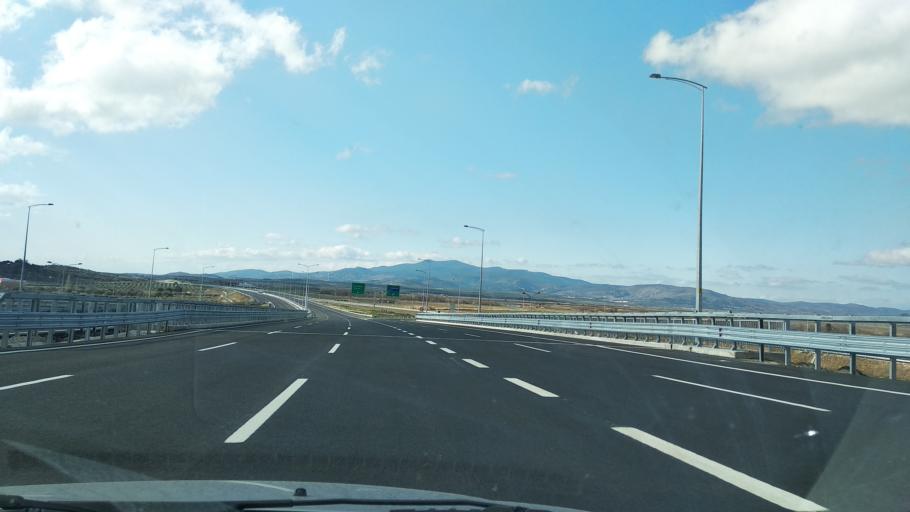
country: TR
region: Izmir
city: Zeytindag
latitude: 38.9733
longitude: 27.0456
